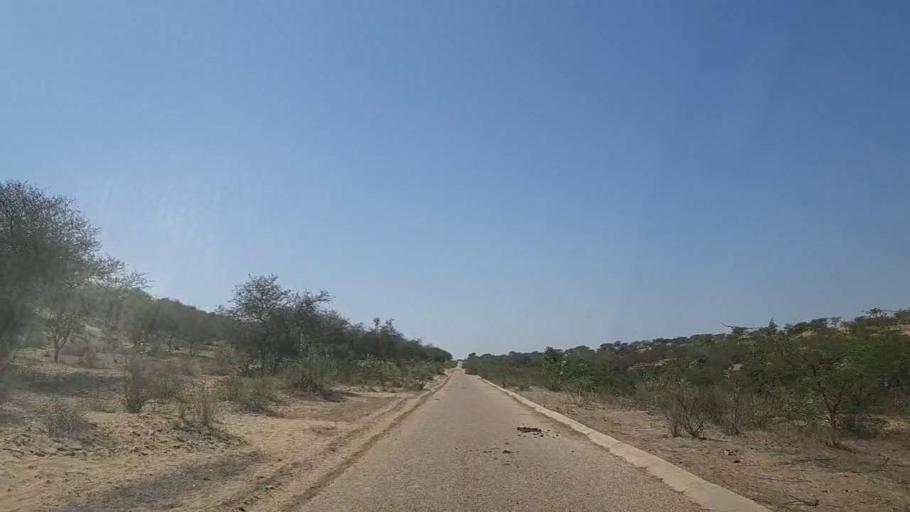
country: PK
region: Sindh
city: Mithi
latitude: 24.8212
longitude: 69.6697
